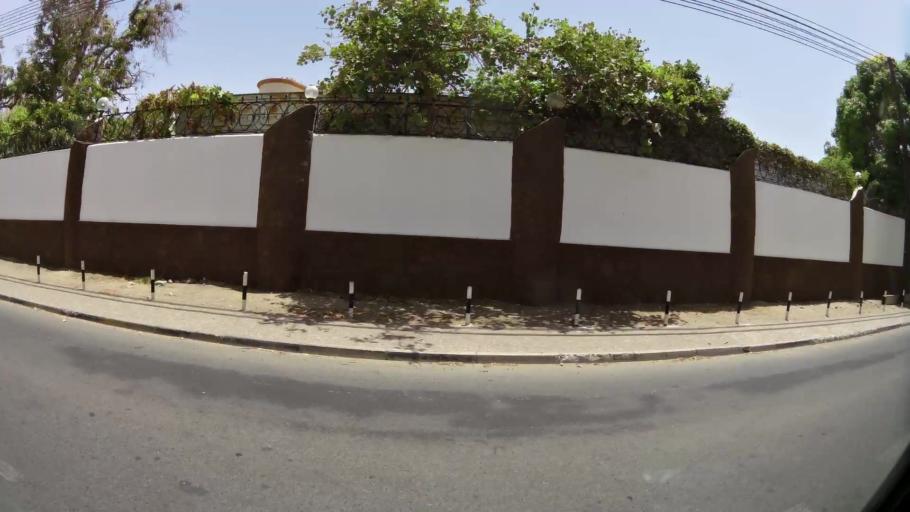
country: OM
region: Muhafazat Masqat
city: Muscat
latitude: 23.6207
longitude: 58.4949
